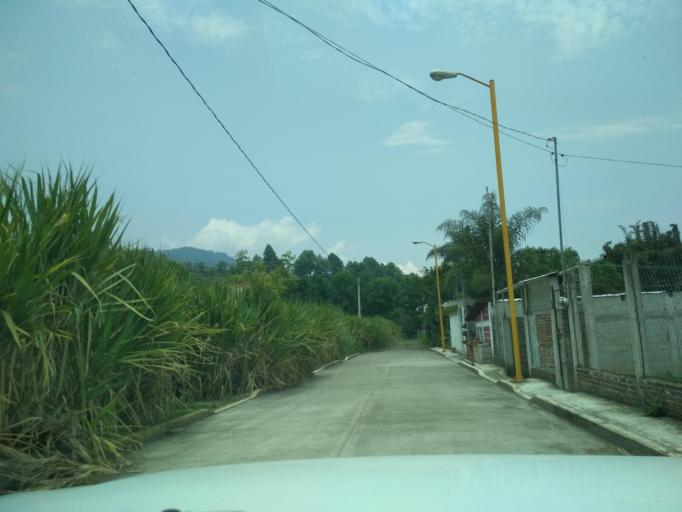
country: MX
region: Veracruz
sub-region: Mariano Escobedo
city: Mariano Escobedo
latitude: 18.9104
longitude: -97.1258
